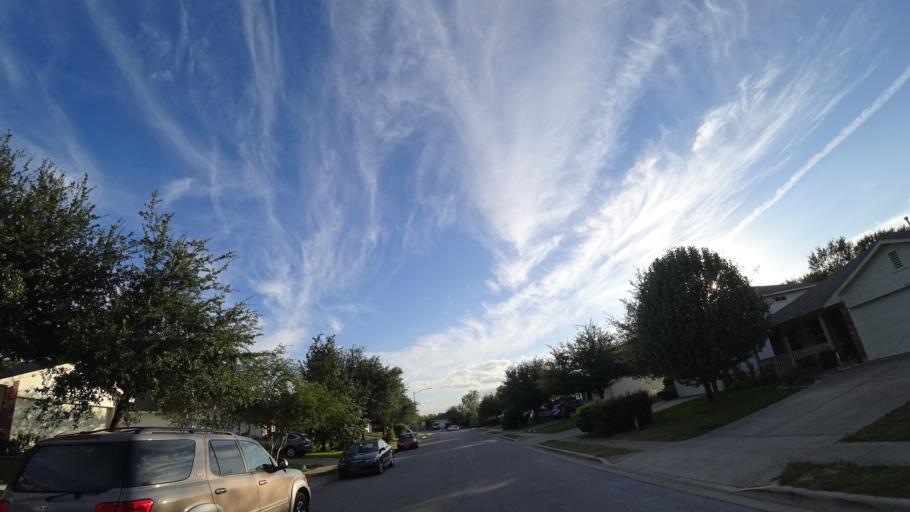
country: US
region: Texas
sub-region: Travis County
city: Austin
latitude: 30.2103
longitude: -97.7625
